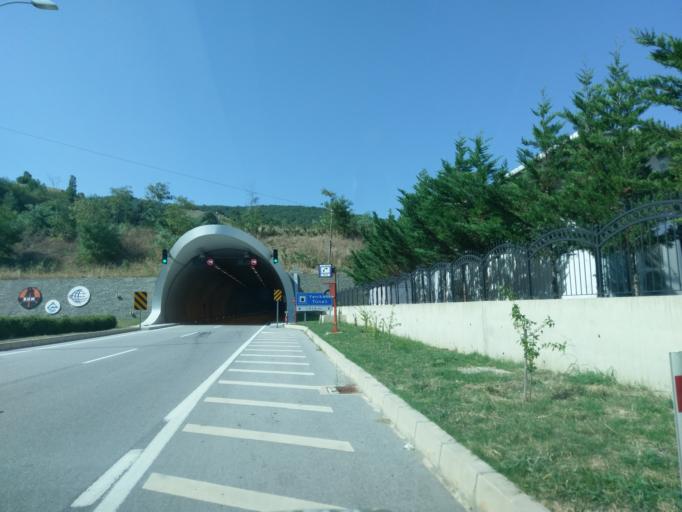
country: TR
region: Sinop
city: Dikmen
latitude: 41.7305
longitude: 35.2617
